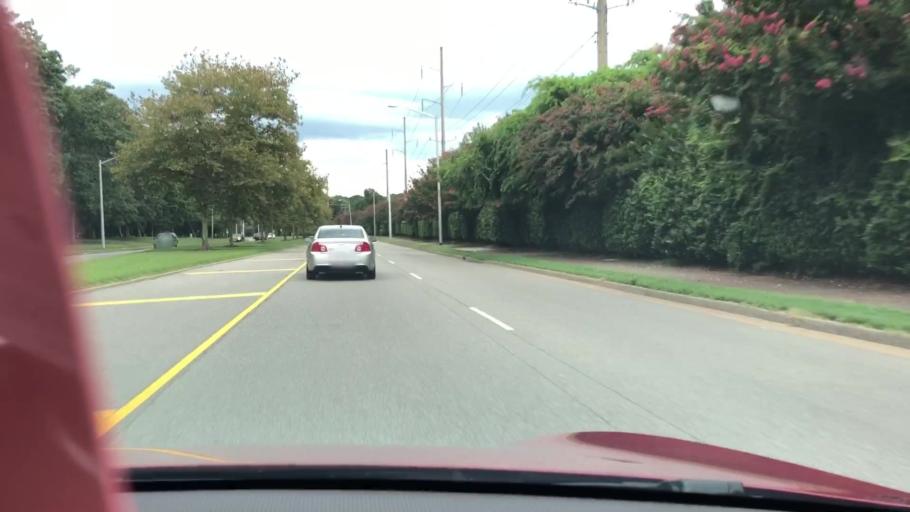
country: US
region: Virginia
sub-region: City of Virginia Beach
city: Virginia Beach
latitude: 36.8867
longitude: -76.0491
